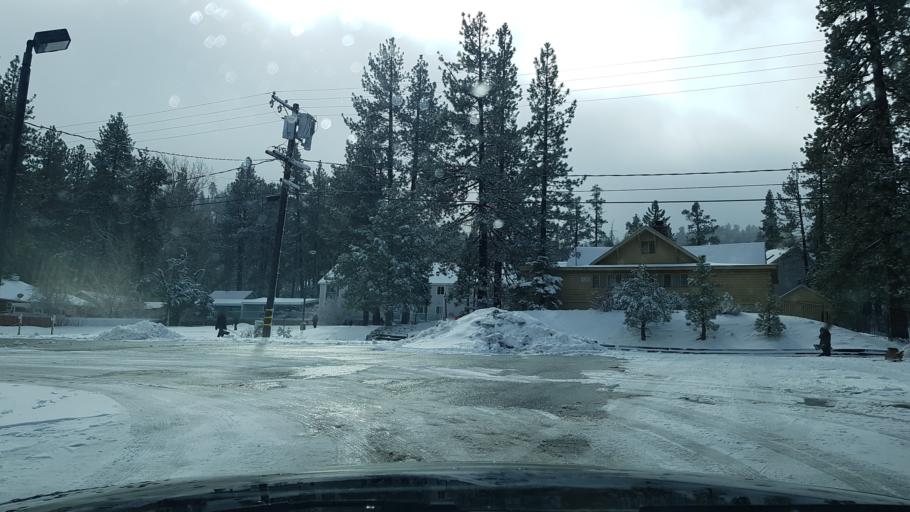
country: US
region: California
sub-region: San Bernardino County
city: Big Bear Lake
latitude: 34.2396
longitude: -116.9125
